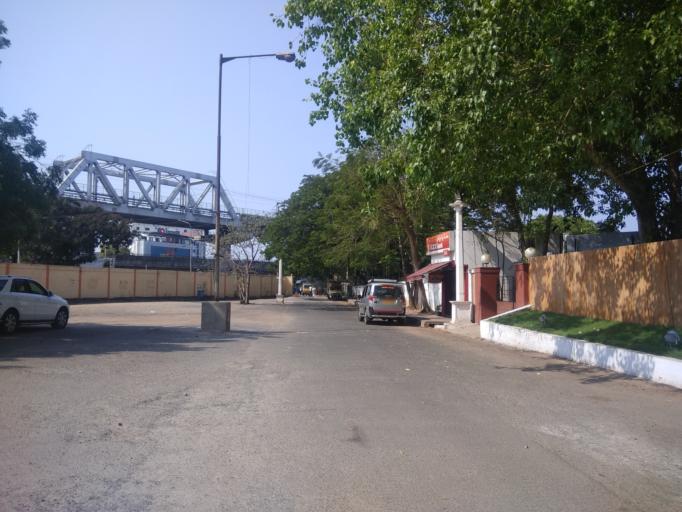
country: IN
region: Tamil Nadu
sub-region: Kancheepuram
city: Alandur
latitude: 13.0087
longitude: 80.2144
